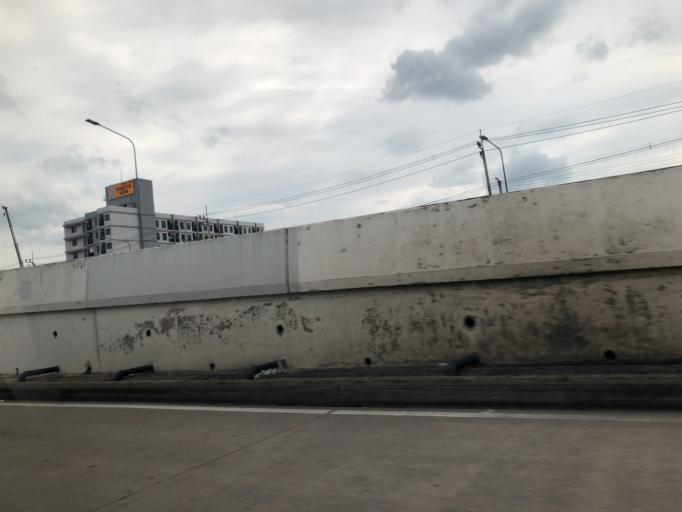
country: TH
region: Nonthaburi
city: Pak Kret
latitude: 13.9084
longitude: 100.5172
